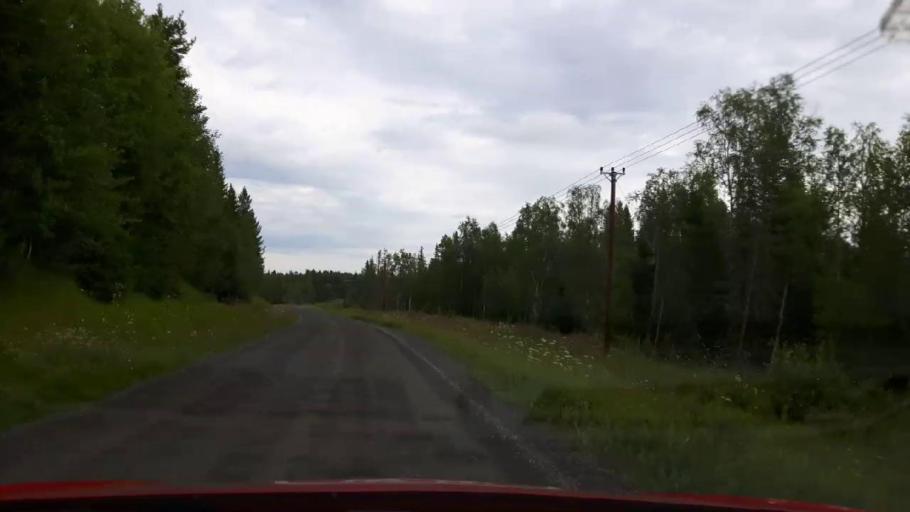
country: SE
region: Jaemtland
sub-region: Stroemsunds Kommun
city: Stroemsund
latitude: 63.4723
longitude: 15.2906
